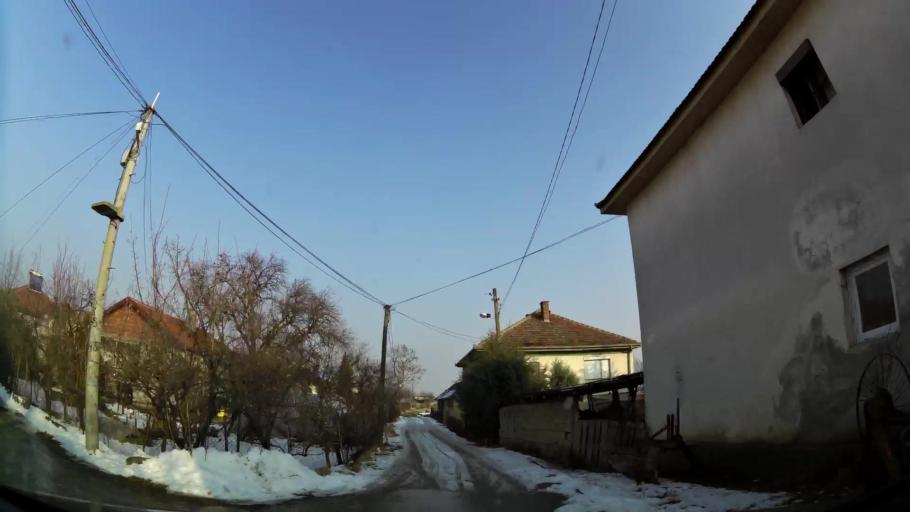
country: MK
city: Kadino
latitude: 41.9668
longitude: 21.6016
